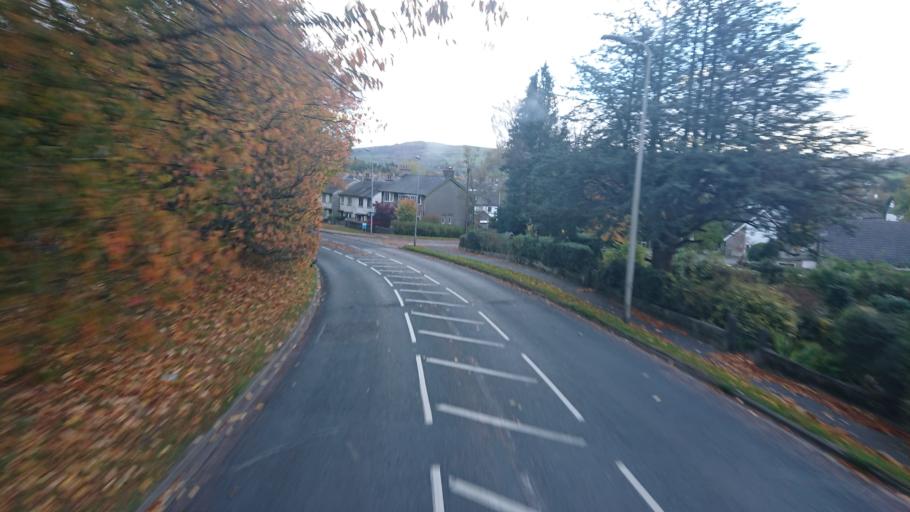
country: GB
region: England
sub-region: Cumbria
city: Kendal
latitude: 54.3149
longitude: -2.7481
